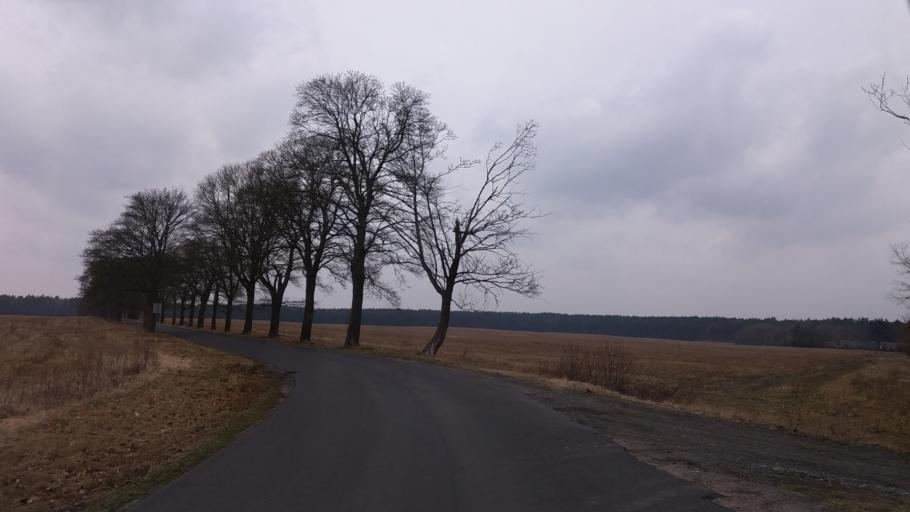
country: PL
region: West Pomeranian Voivodeship
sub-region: Powiat choszczenski
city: Drawno
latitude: 53.1695
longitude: 15.6842
